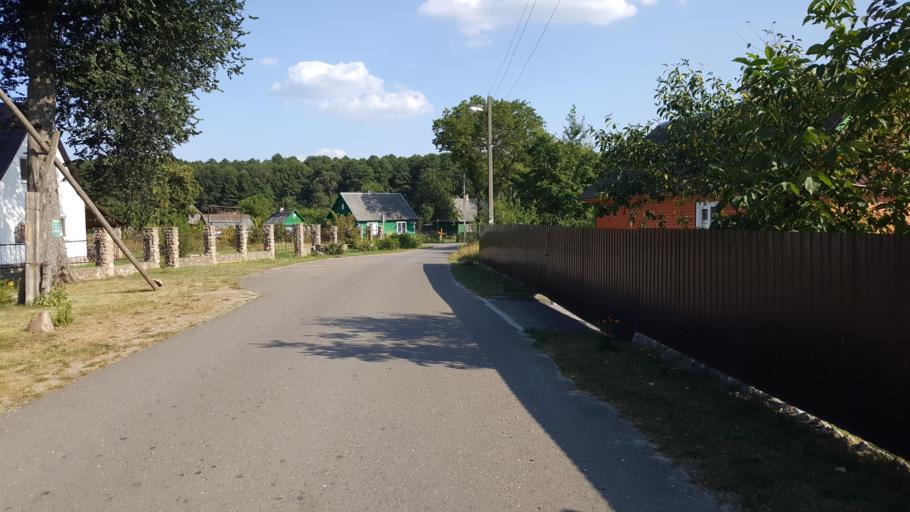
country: BY
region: Brest
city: Kamyanyuki
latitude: 52.5505
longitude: 23.6519
